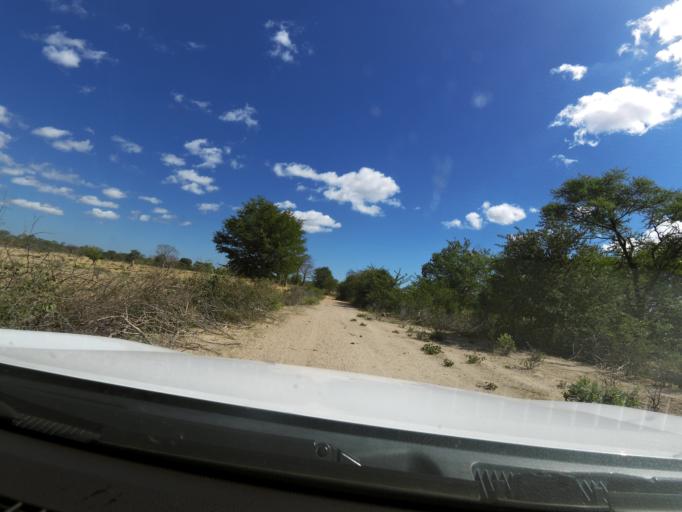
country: ZW
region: Matabeleland North
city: Kamativi Mine
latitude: -17.9954
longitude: 27.1295
